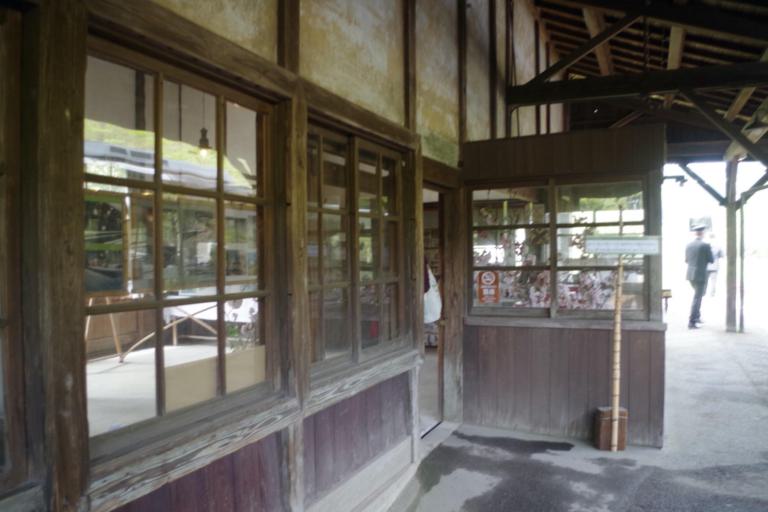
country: JP
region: Kagoshima
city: Kokubu-matsuki
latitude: 31.8267
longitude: 130.7228
